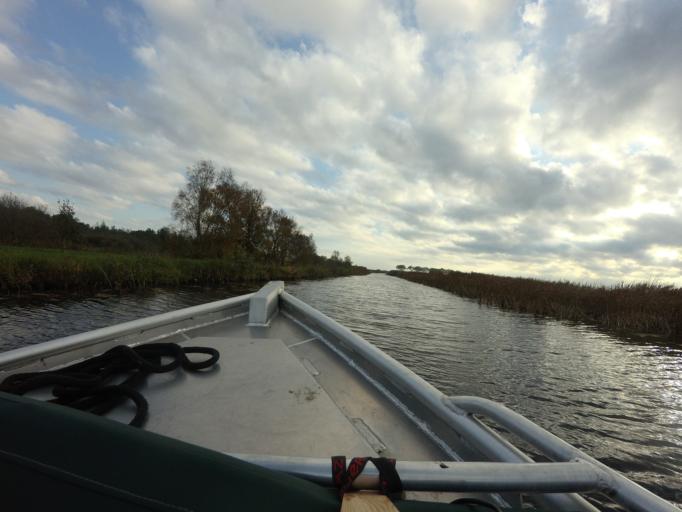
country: NL
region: Overijssel
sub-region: Gemeente Steenwijkerland
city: Blokzijl
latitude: 52.7429
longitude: 5.9751
